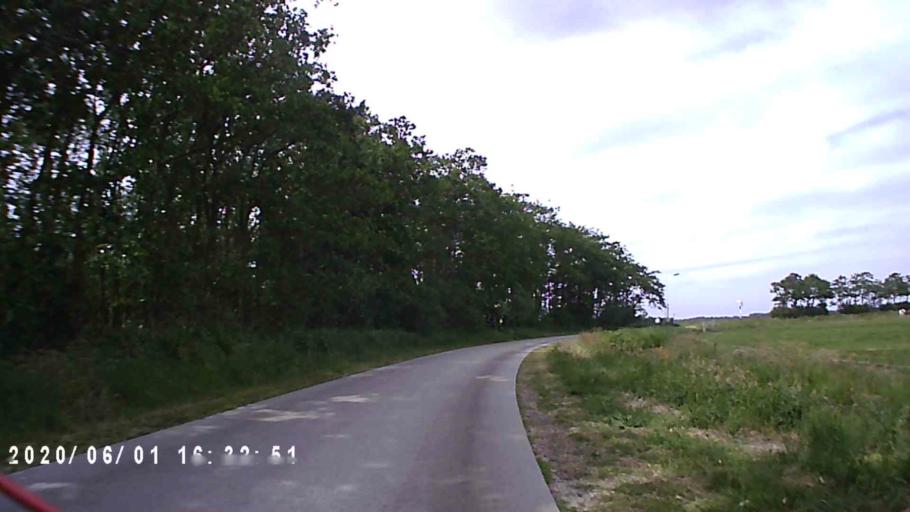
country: NL
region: Friesland
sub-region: Gemeente Leeuwarden
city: Camminghaburen
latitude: 53.1909
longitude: 5.8642
